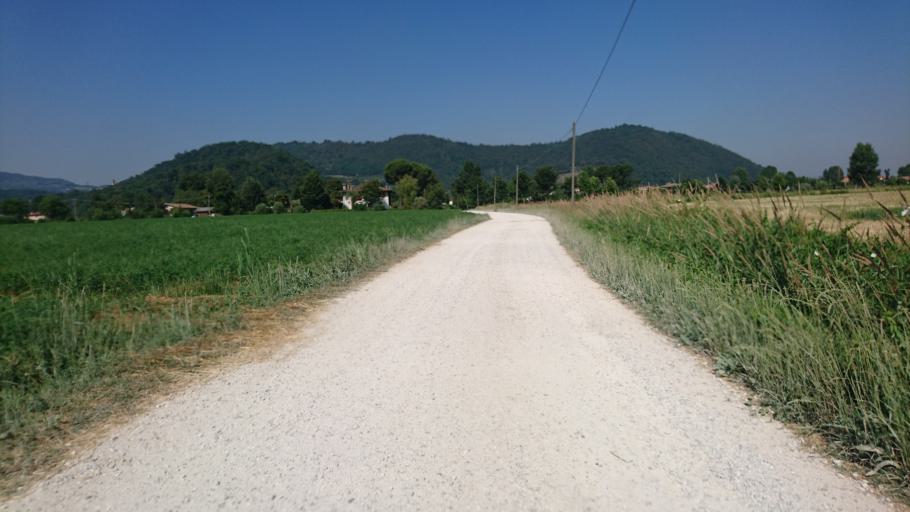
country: IT
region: Veneto
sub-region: Provincia di Padova
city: San Biagio
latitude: 45.3612
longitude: 11.7503
